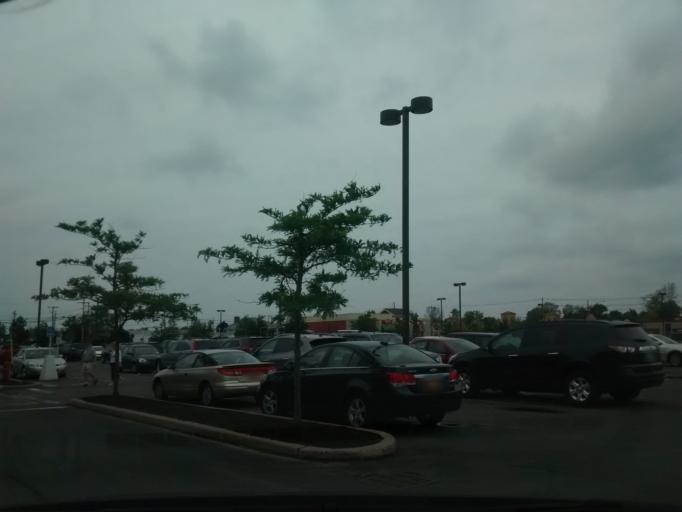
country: US
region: New York
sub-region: Erie County
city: Amherst
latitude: 42.9858
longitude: -78.8209
